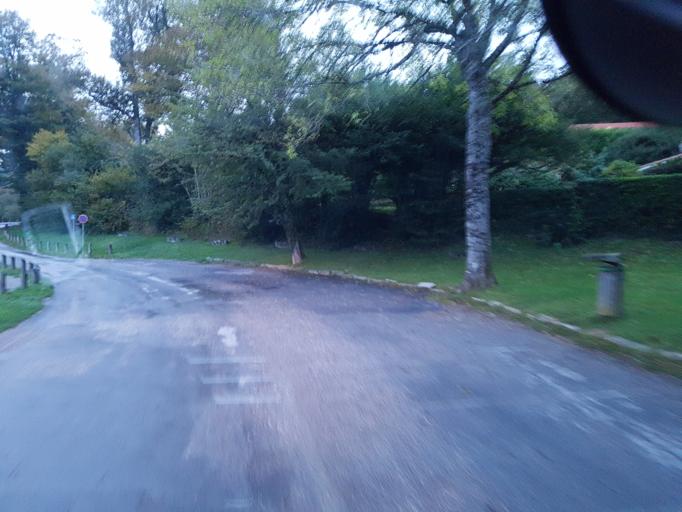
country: FR
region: Midi-Pyrenees
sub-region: Departement du Tarn
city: Mazamet
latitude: 43.4656
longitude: 2.3442
